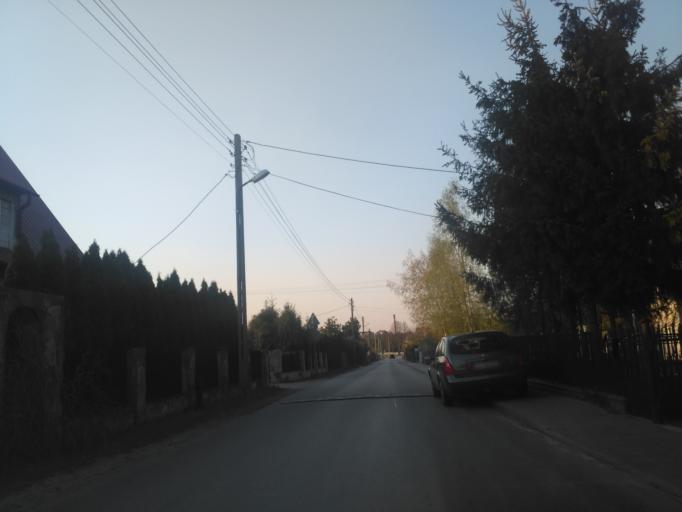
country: PL
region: Lublin Voivodeship
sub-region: Powiat chelmski
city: Pokrowka
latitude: 51.1154
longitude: 23.4840
